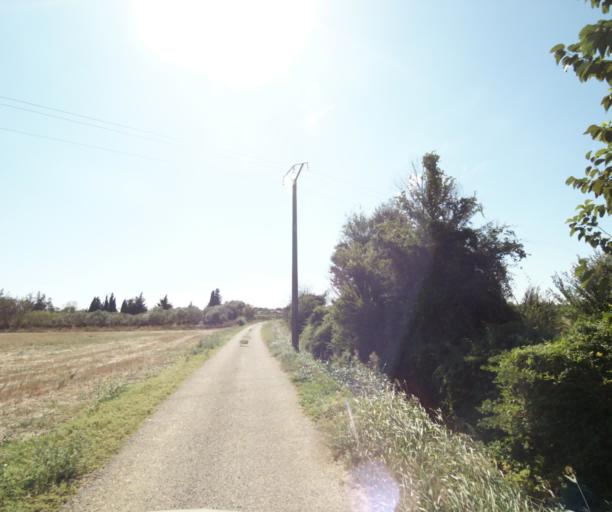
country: FR
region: Languedoc-Roussillon
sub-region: Departement du Gard
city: Bouillargues
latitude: 43.8089
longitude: 4.4245
